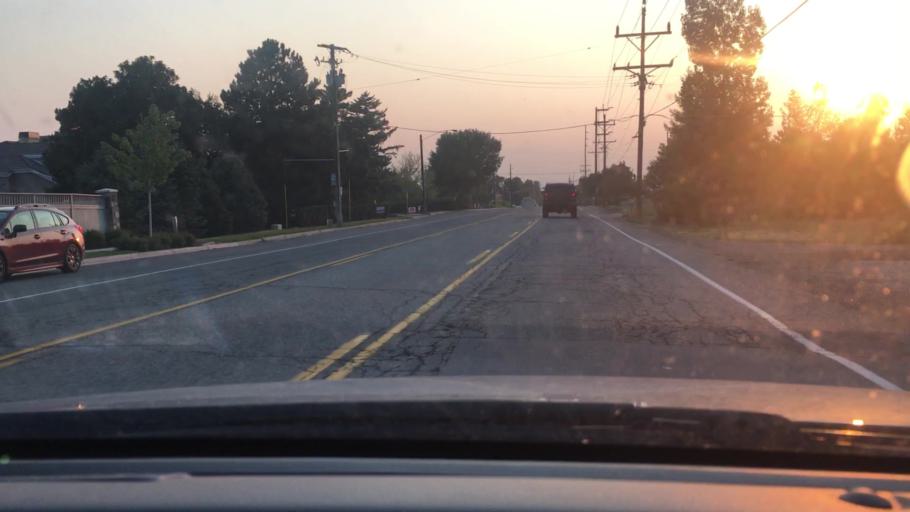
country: US
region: Utah
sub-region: Salt Lake County
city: East Millcreek
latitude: 40.6871
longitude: -111.8213
